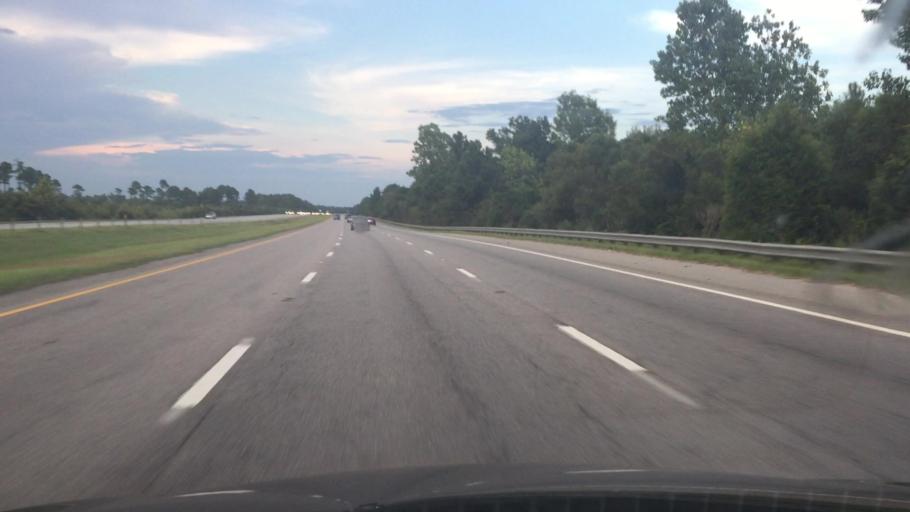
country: US
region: South Carolina
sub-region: Horry County
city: Myrtle Beach
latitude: 33.7713
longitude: -78.8222
